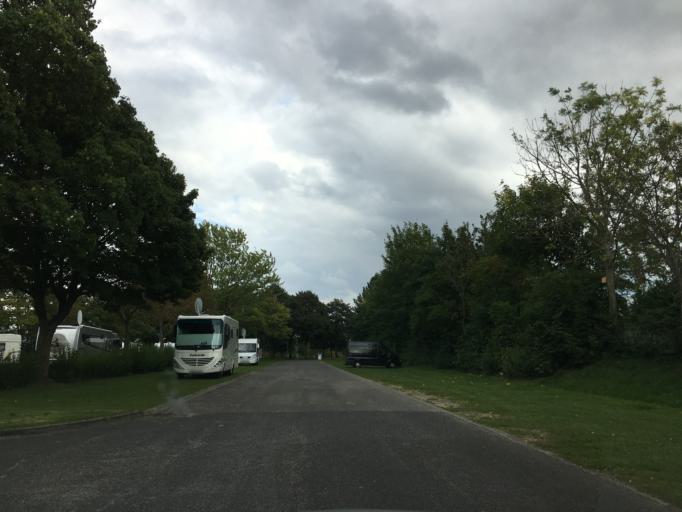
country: DE
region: Schleswig-Holstein
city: Laboe
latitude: 54.4104
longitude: 10.2309
